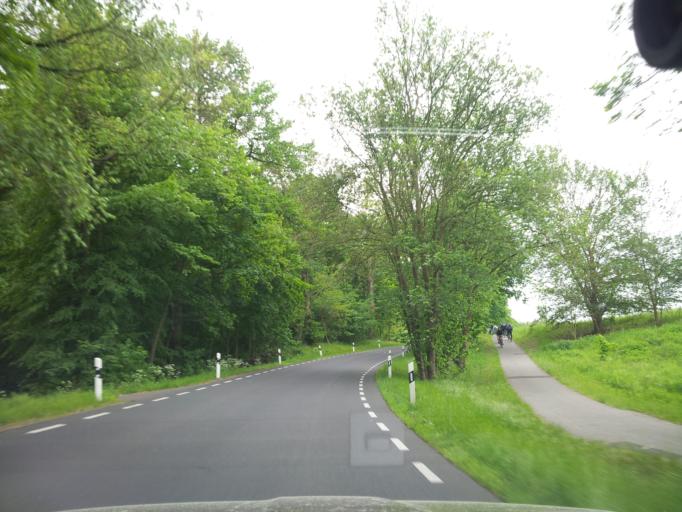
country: DE
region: Brandenburg
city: Werder
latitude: 52.3386
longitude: 12.9403
